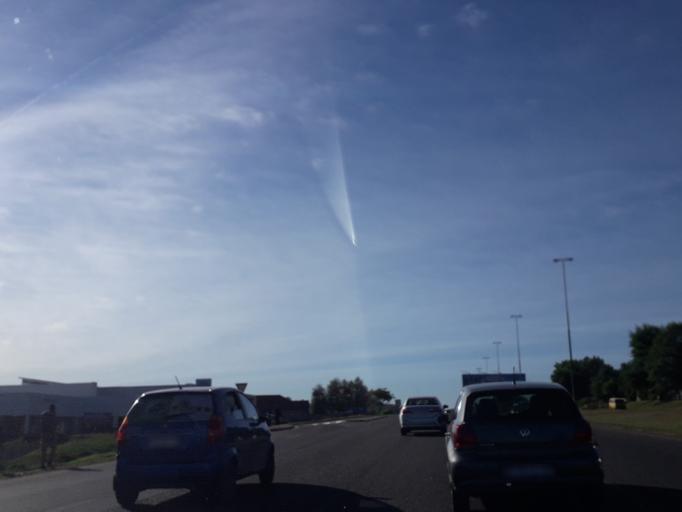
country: ZA
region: Gauteng
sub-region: City of Johannesburg Metropolitan Municipality
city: Roodepoort
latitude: -26.1356
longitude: 27.9160
